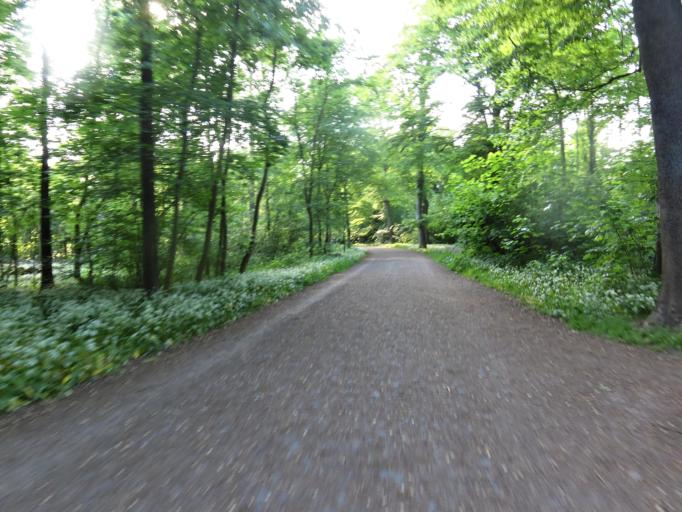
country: DE
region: Saxony
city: Leipzig
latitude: 51.3278
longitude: 12.3527
